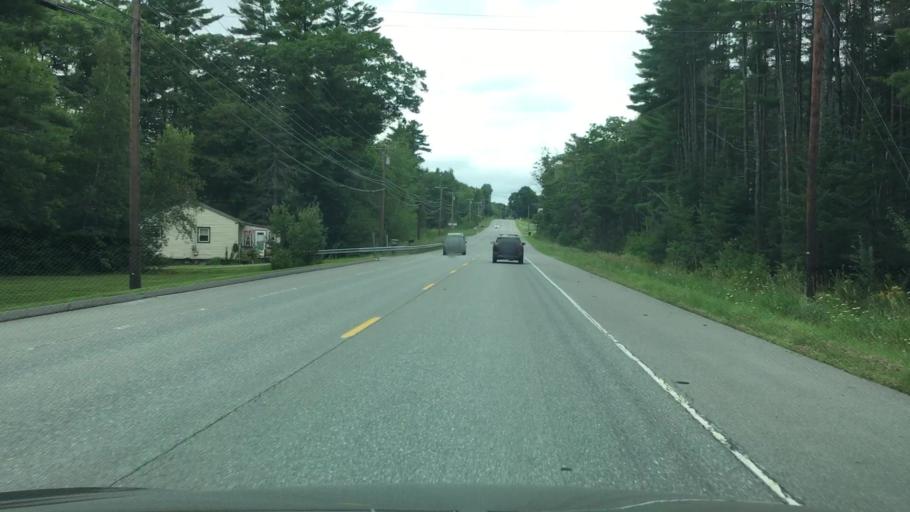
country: US
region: Maine
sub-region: Penobscot County
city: Orrington
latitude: 44.7071
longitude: -68.8240
